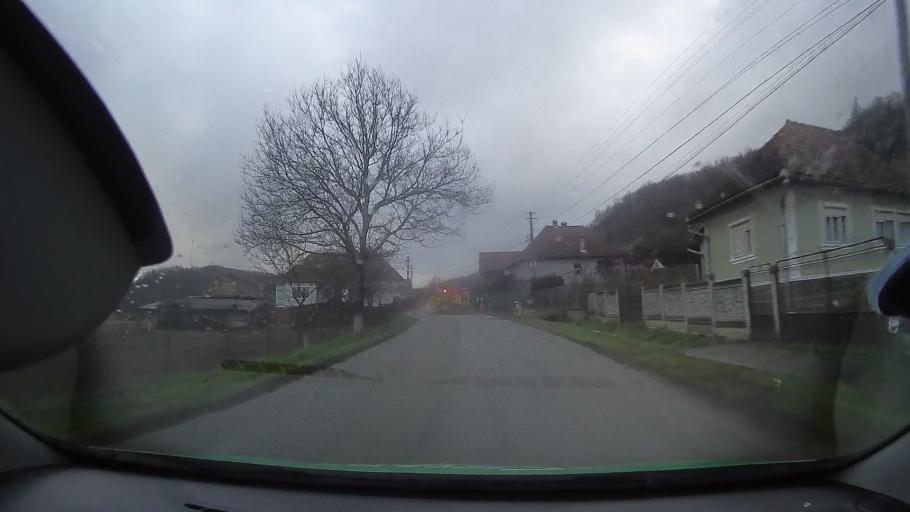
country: RO
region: Hunedoara
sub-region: Comuna Baia de Cris
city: Baia de Cris
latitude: 46.2113
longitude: 22.7154
